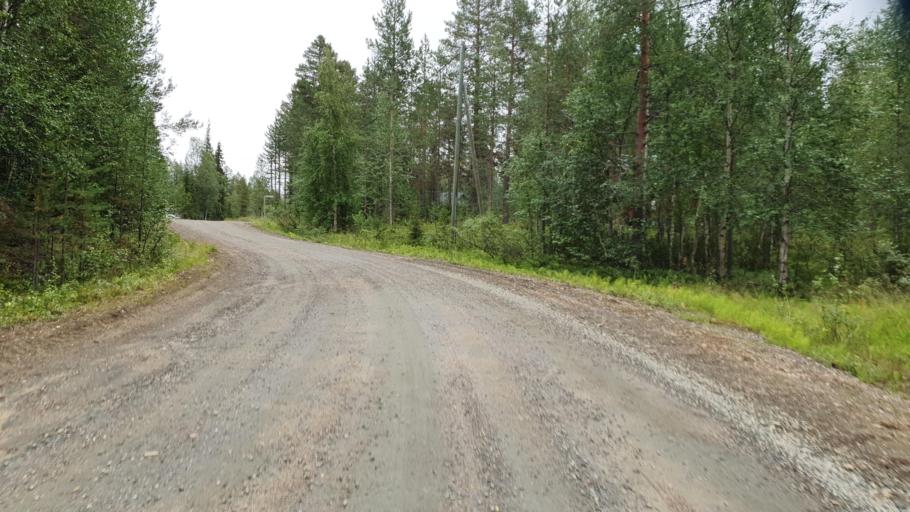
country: FI
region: Lapland
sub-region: Tunturi-Lappi
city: Kolari
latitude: 67.6023
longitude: 24.1842
